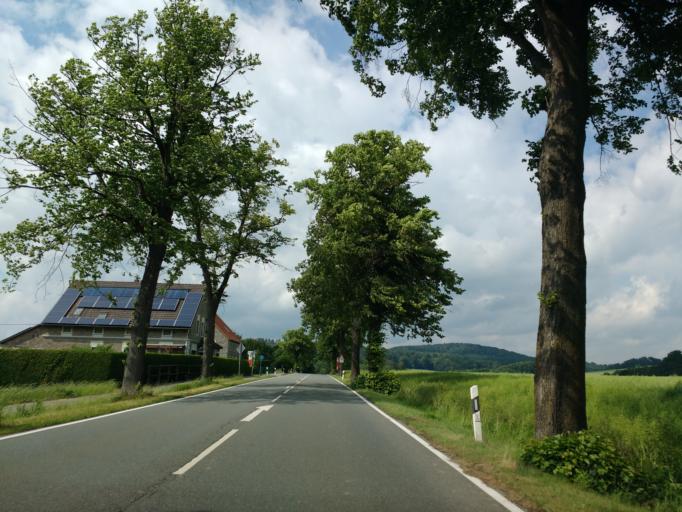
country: DE
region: North Rhine-Westphalia
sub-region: Regierungsbezirk Detmold
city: Lemgo
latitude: 52.0572
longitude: 8.9071
